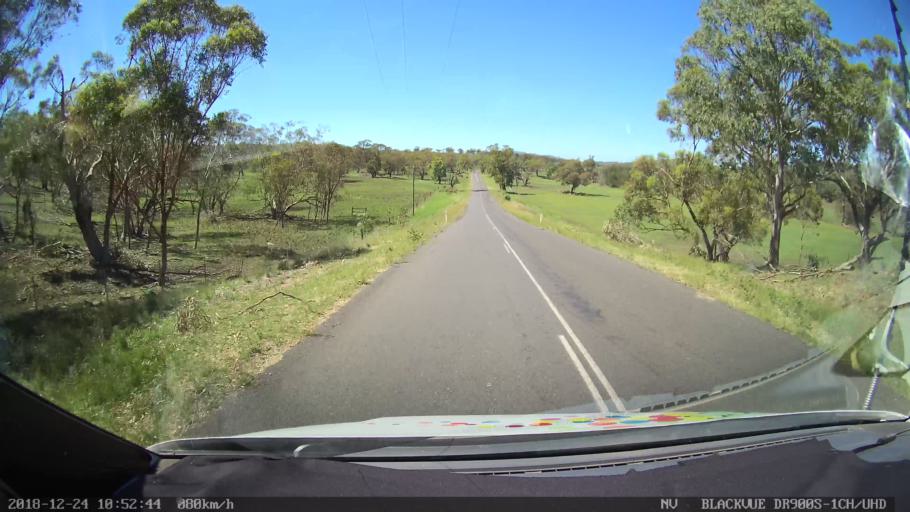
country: AU
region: New South Wales
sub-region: Upper Hunter Shire
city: Merriwa
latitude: -31.9838
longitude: 150.4225
